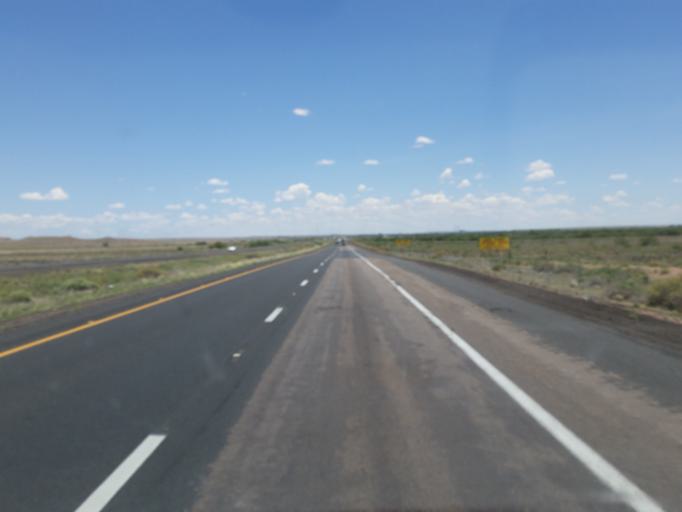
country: US
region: Arizona
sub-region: Navajo County
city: Joseph City
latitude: 34.9712
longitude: -110.4724
